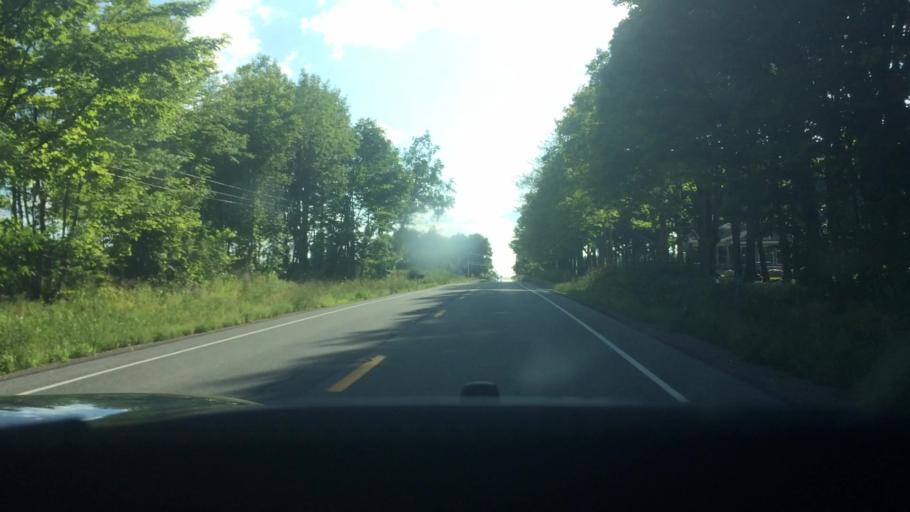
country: US
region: New York
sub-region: Franklin County
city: Malone
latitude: 44.7397
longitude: -74.5848
